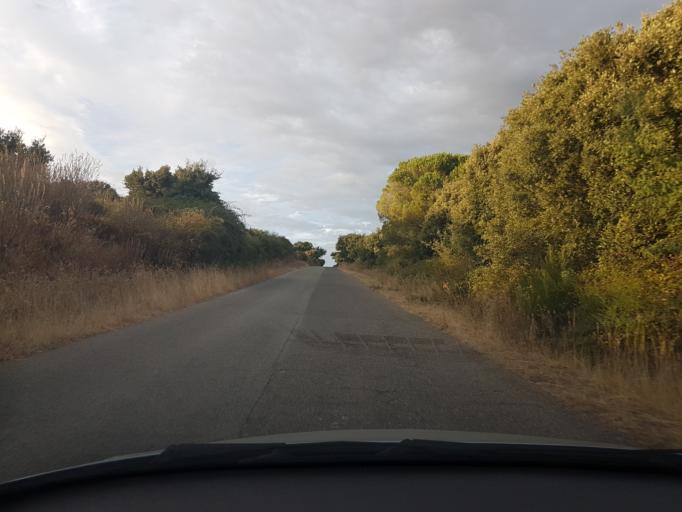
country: IT
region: Sardinia
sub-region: Provincia di Oristano
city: Seneghe
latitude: 40.1014
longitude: 8.6211
